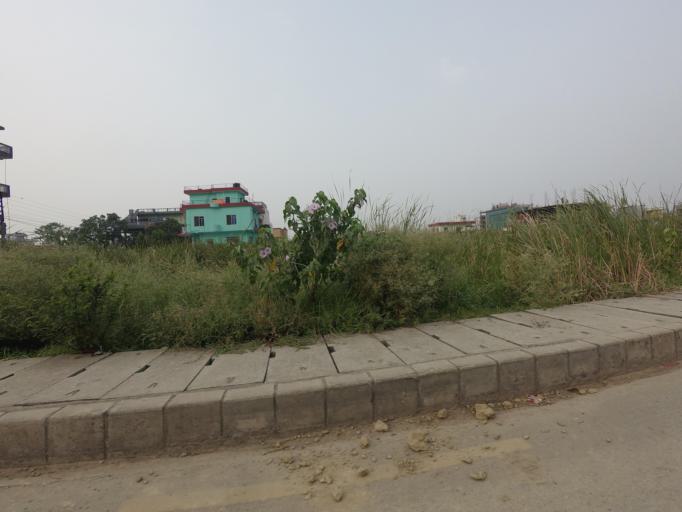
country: NP
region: Western Region
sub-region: Lumbini Zone
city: Bhairahawa
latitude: 27.5207
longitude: 83.4497
